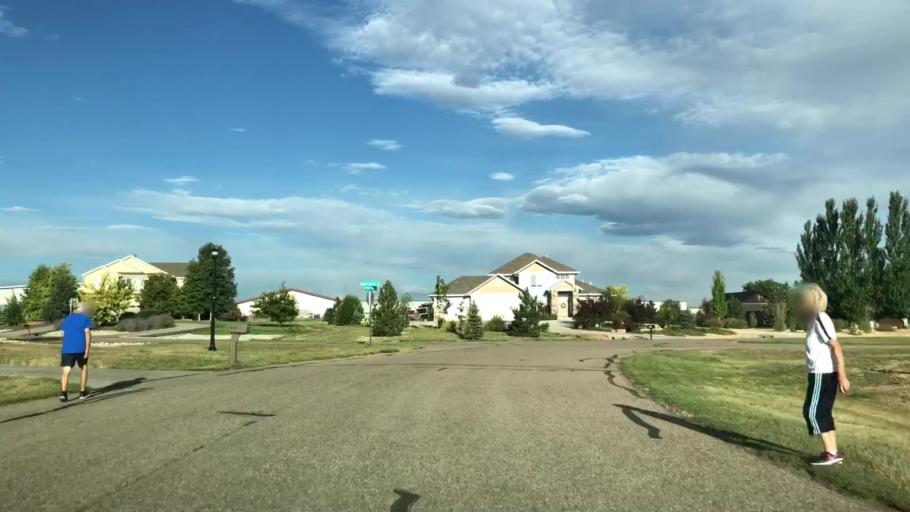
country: US
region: Colorado
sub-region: Weld County
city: Windsor
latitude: 40.4377
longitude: -104.9608
